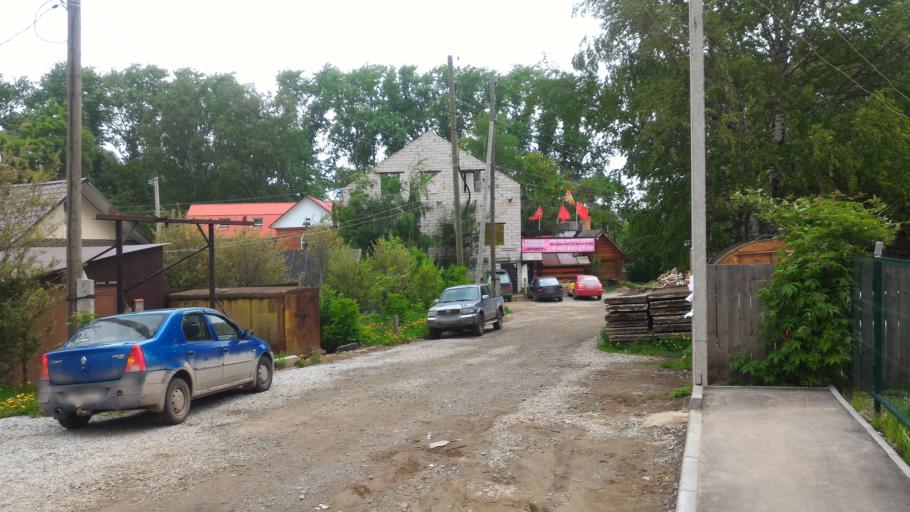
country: RU
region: Perm
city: Perm
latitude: 57.9900
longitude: 56.2241
